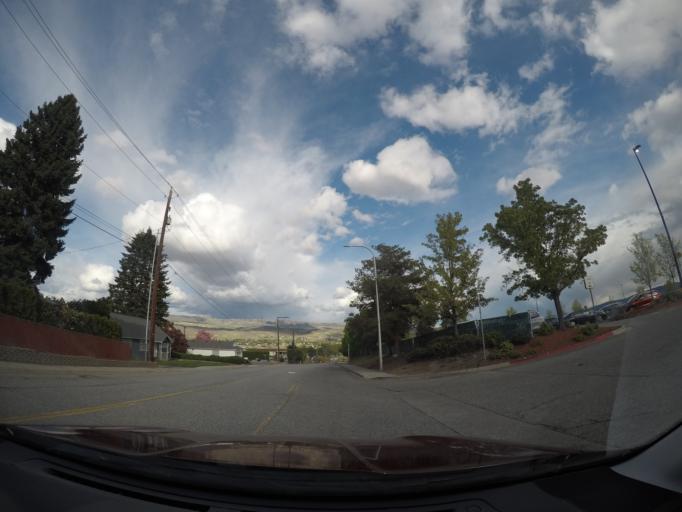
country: US
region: Washington
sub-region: Chelan County
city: Sunnyslope
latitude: 47.4551
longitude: -120.3388
